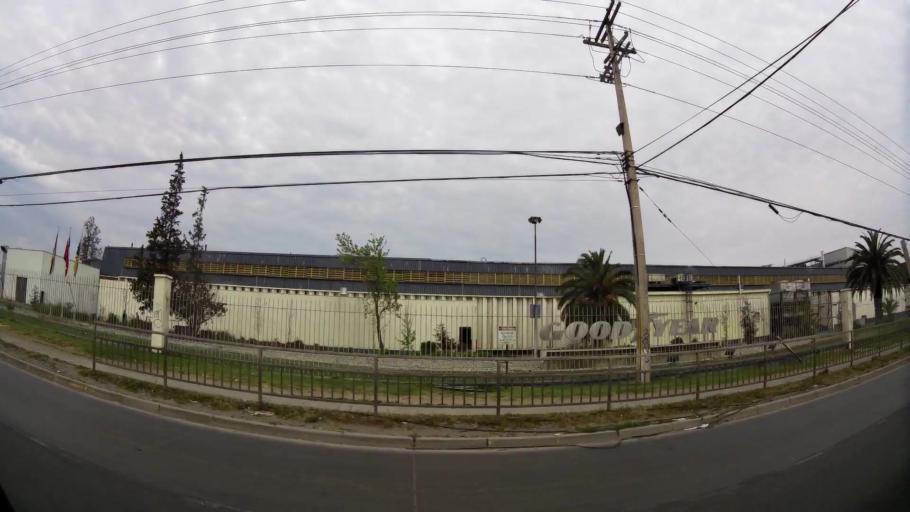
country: CL
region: Santiago Metropolitan
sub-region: Provincia de Maipo
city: San Bernardo
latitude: -33.5292
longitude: -70.7595
